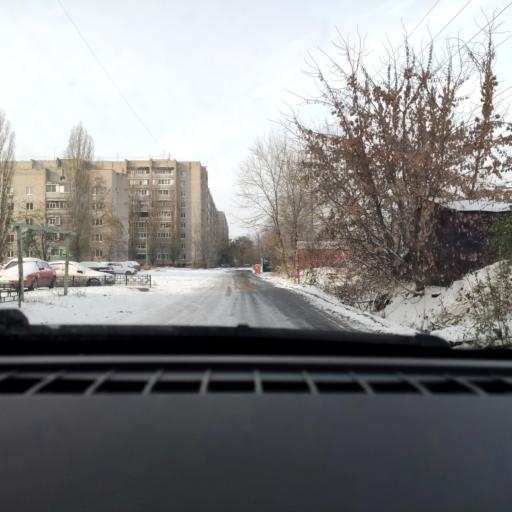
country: RU
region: Voronezj
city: Voronezh
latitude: 51.6438
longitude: 39.2759
